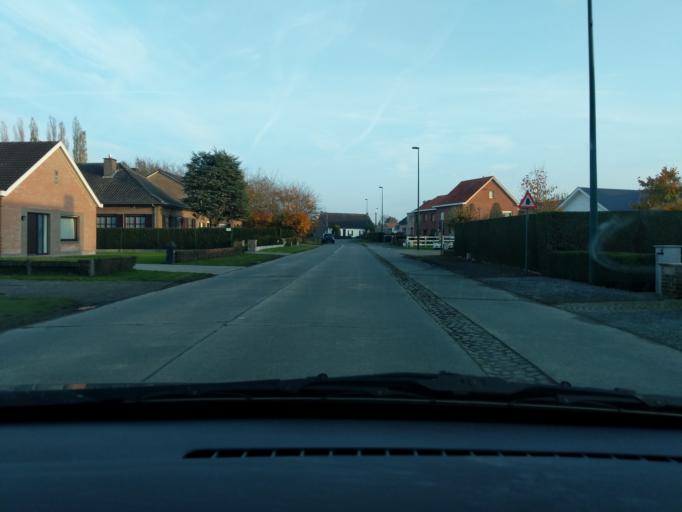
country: BE
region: Flanders
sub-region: Provincie Oost-Vlaanderen
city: Aalter
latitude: 51.0456
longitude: 3.4730
